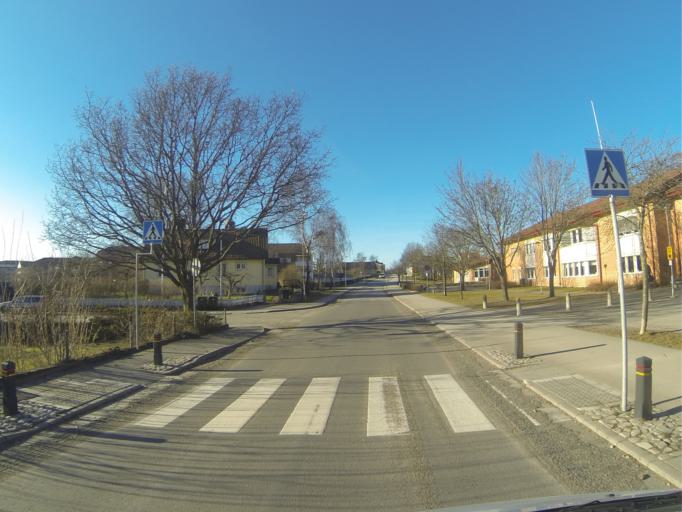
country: SE
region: Skane
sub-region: Hoors Kommun
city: Hoeoer
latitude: 55.9356
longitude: 13.5474
